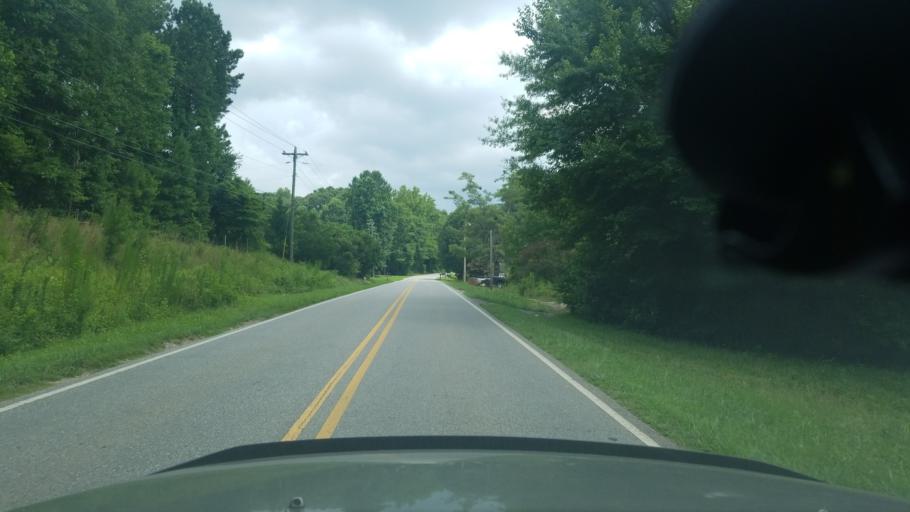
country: US
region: Georgia
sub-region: Forsyth County
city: Cumming
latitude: 34.3034
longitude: -84.1573
